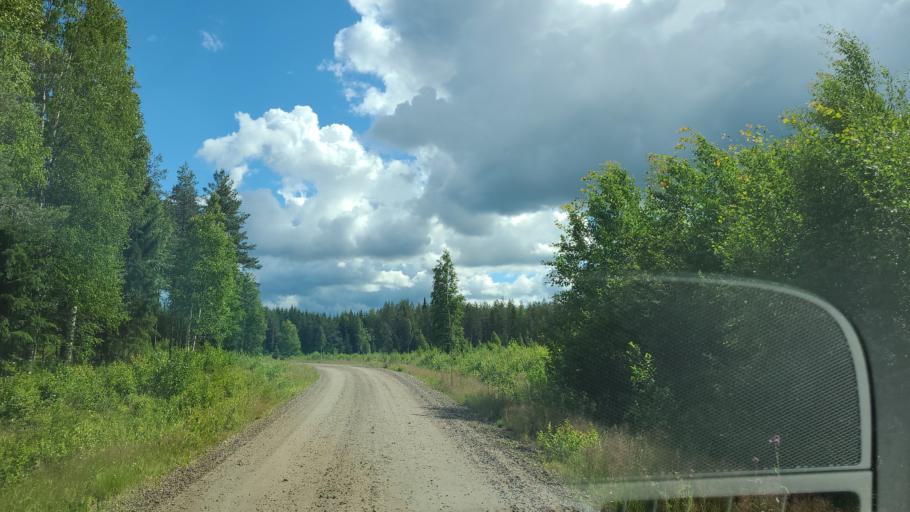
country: FI
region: Northern Savo
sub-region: Koillis-Savo
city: Kaavi
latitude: 63.0273
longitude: 28.7794
